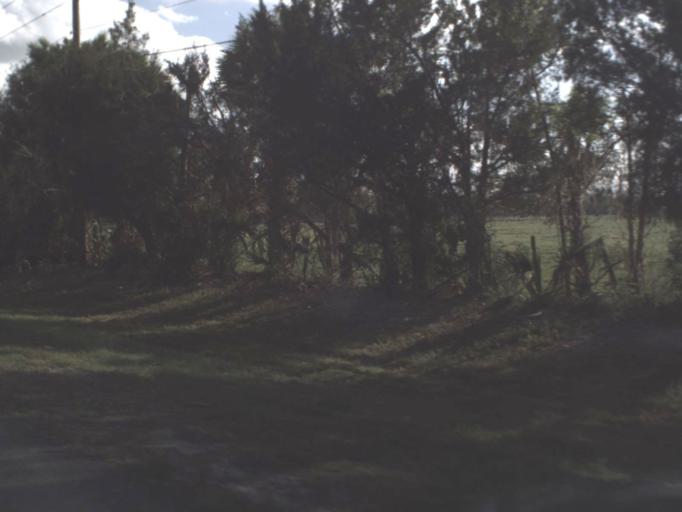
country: US
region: Florida
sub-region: Flagler County
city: Bunnell
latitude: 29.3428
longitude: -81.3110
